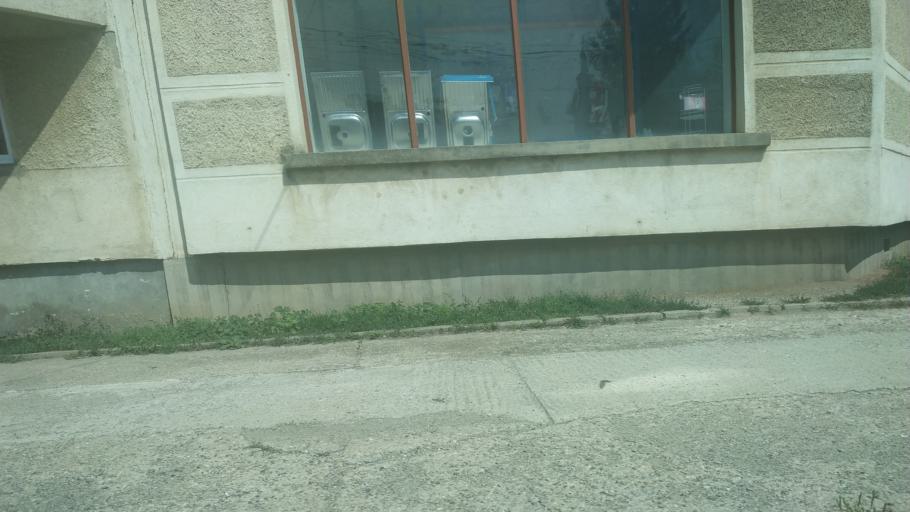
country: RO
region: Brasov
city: Fogarasch
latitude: 45.8398
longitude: 24.9668
